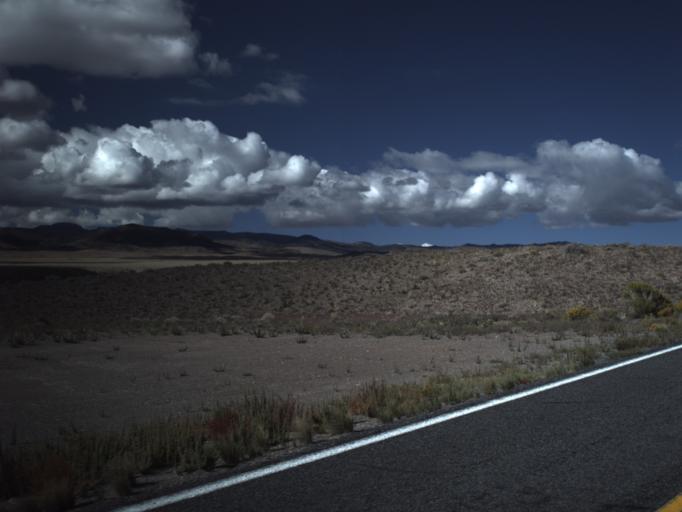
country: US
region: Utah
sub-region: Beaver County
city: Milford
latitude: 38.5686
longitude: -113.7802
